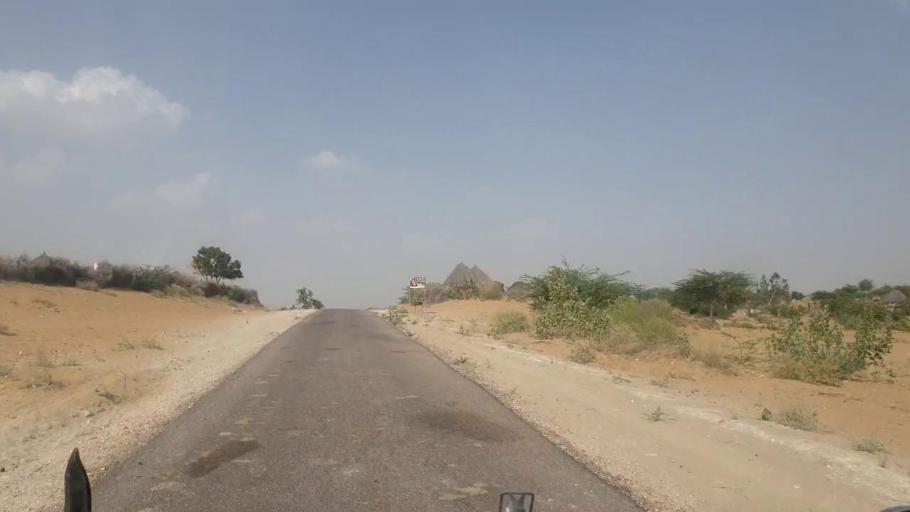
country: PK
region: Sindh
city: Islamkot
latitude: 25.2145
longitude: 70.2851
